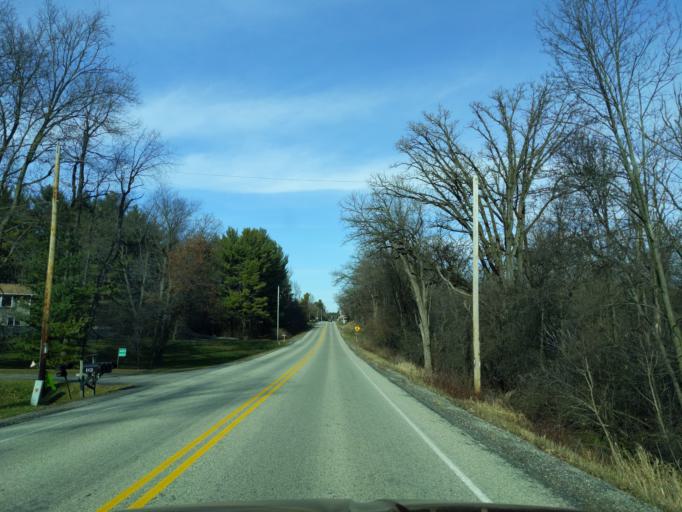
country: US
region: Wisconsin
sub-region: Jefferson County
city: Palmyra
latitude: 42.7962
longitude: -88.6025
